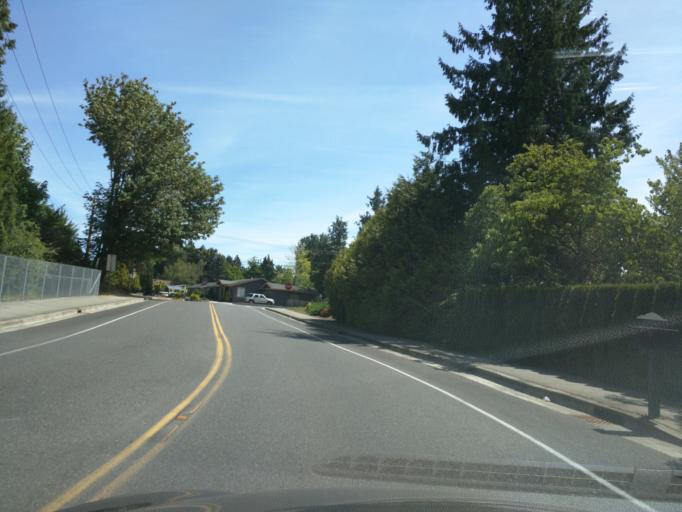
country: US
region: Washington
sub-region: Whatcom County
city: Lynden
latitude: 48.9439
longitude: -122.4647
